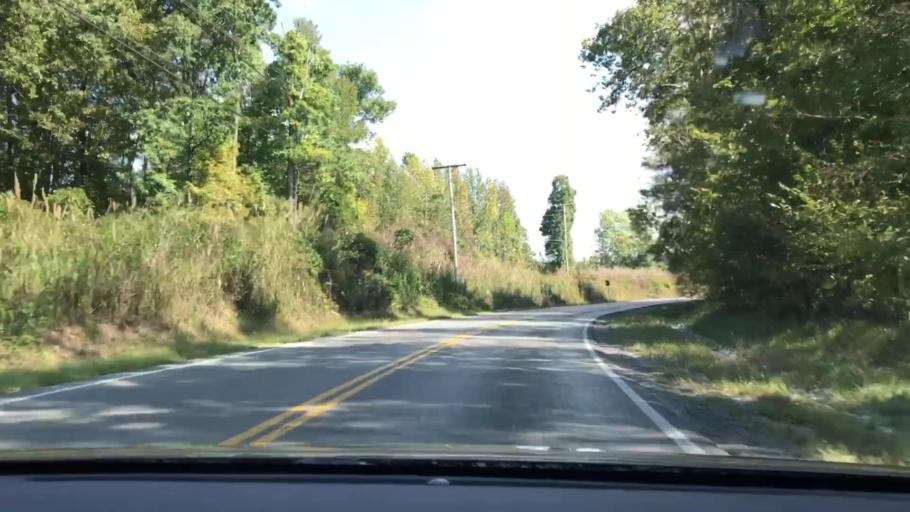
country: US
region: Kentucky
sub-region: Trigg County
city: Cadiz
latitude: 36.8108
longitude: -87.8997
